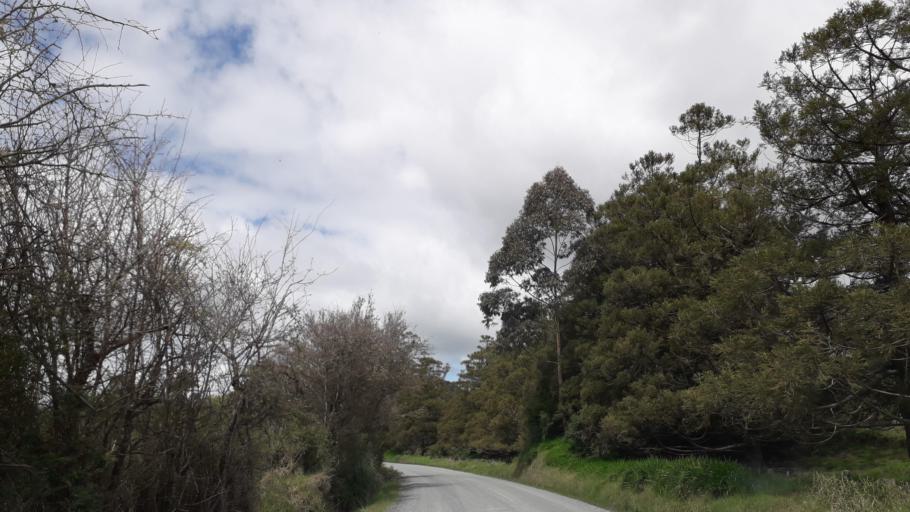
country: NZ
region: Northland
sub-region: Far North District
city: Taipa
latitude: -35.0880
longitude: 173.5122
